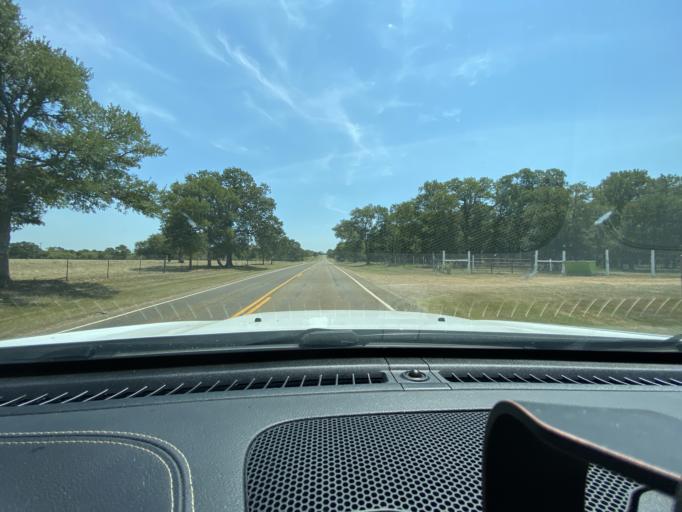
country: US
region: Texas
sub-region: Lee County
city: Giddings
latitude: 30.1379
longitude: -97.0660
